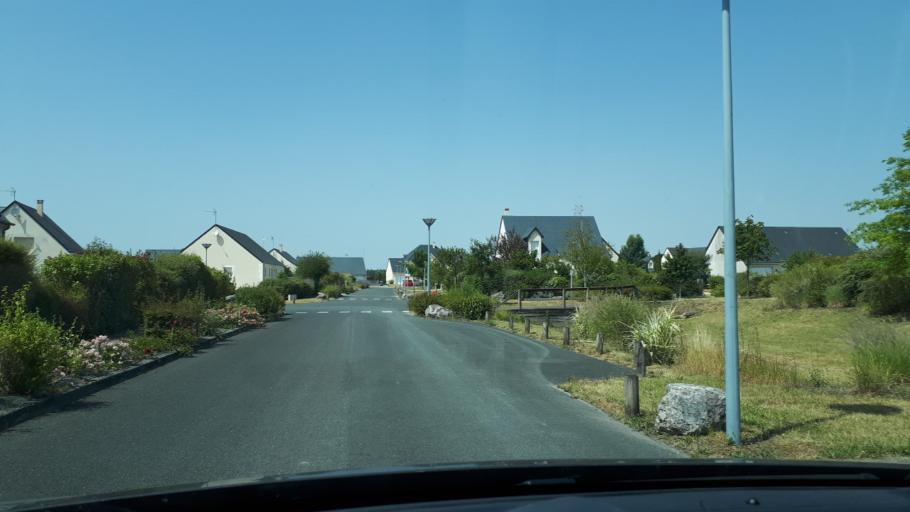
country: FR
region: Centre
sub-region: Departement du Loir-et-Cher
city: Vendome
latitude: 47.8151
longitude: 1.0506
